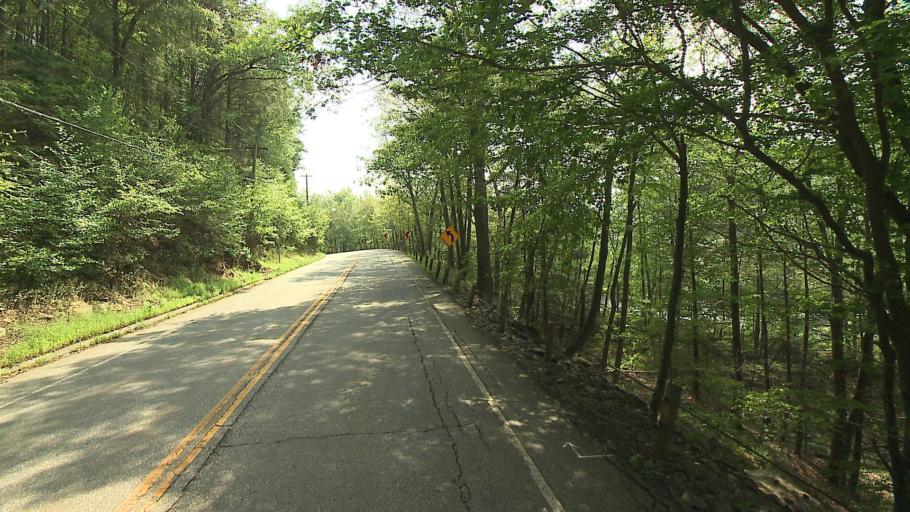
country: US
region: Connecticut
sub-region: Litchfield County
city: Oakville
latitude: 41.6204
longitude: -73.0585
